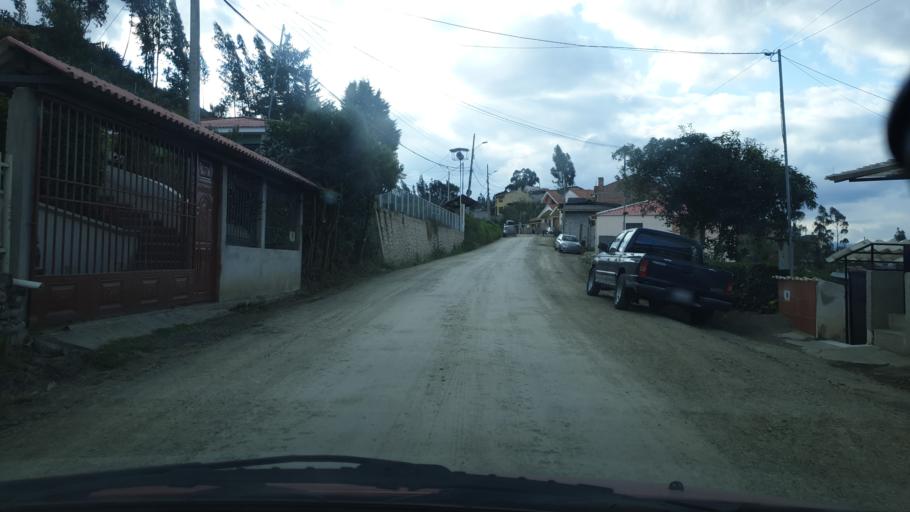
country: EC
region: Azuay
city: Cuenca
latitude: -2.9214
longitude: -78.9748
